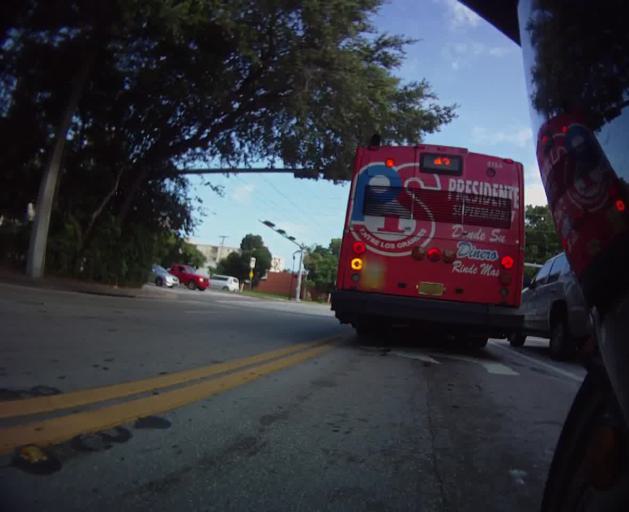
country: US
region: Florida
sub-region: Miami-Dade County
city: Coral Gables
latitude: 25.7351
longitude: -80.2621
